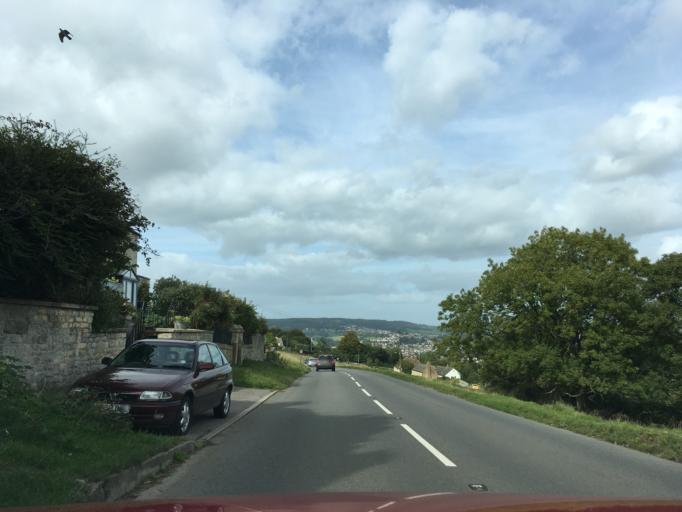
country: GB
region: England
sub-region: Gloucestershire
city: Nailsworth
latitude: 51.7283
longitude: -2.2434
